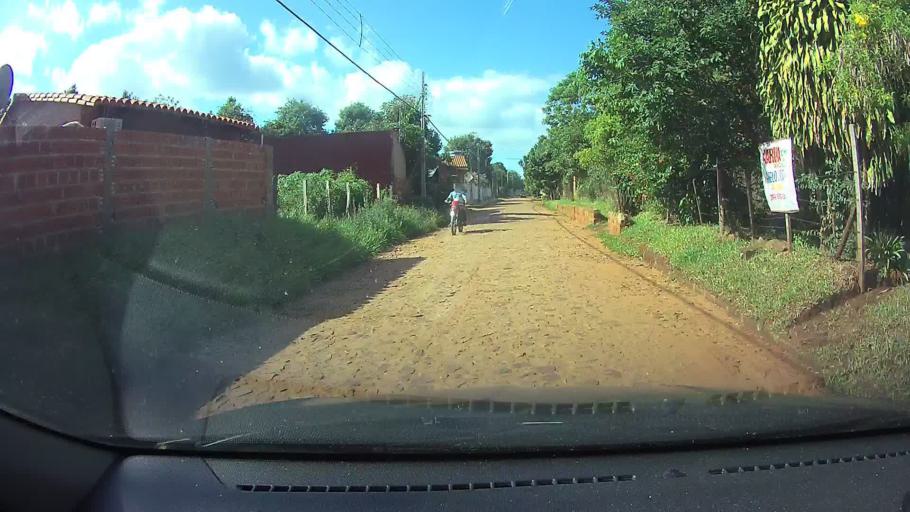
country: PY
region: Central
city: Limpio
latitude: -25.2443
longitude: -57.4673
